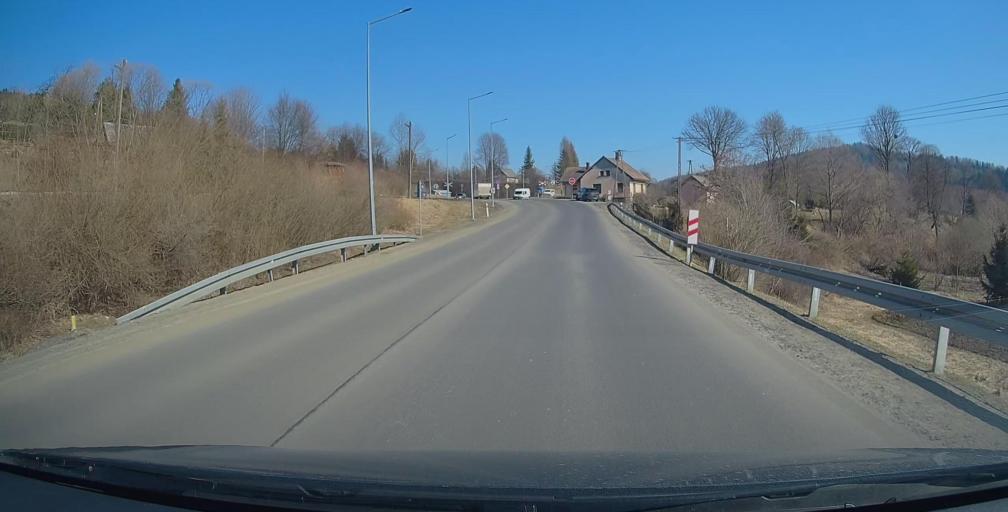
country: PL
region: Subcarpathian Voivodeship
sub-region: Powiat bieszczadzki
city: Ustrzyki Dolne
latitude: 49.4781
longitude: 22.6721
